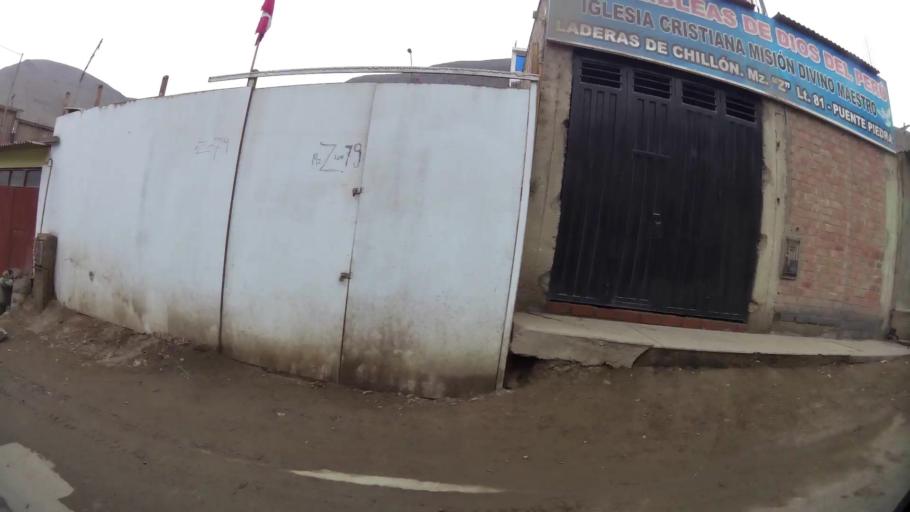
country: PE
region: Lima
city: Ventanilla
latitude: -11.9161
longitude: -77.0930
